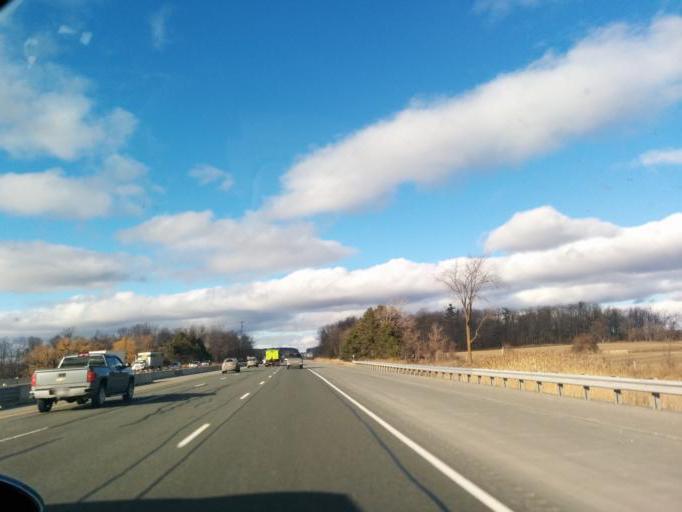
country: CA
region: Ontario
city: Vaughan
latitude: 43.9318
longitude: -79.5685
